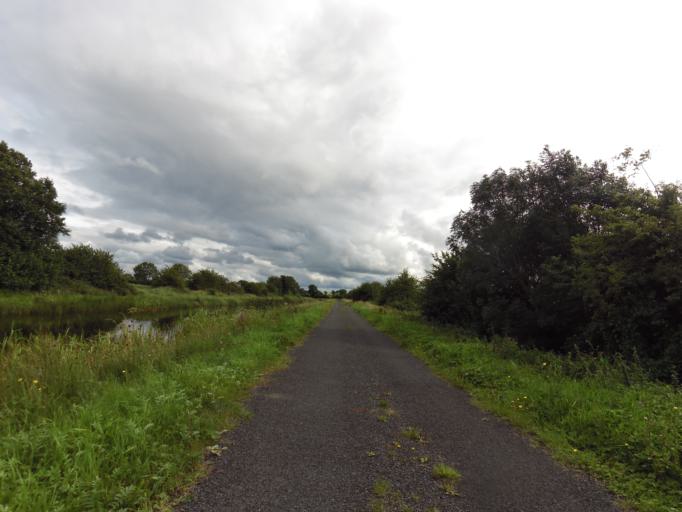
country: IE
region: Leinster
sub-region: An Iarmhi
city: An Muileann gCearr
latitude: 53.5608
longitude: -7.5032
